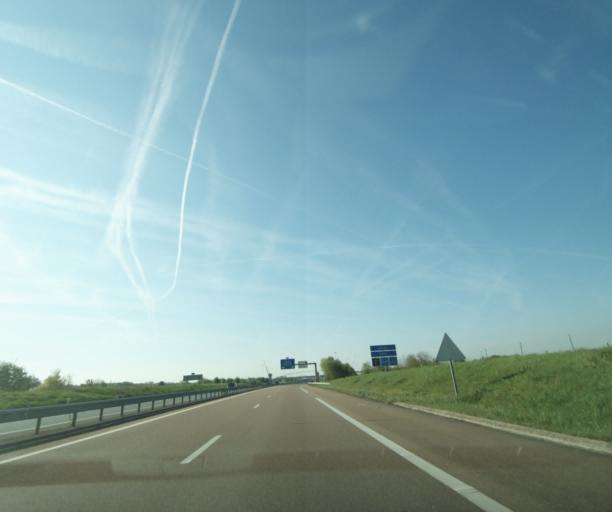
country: FR
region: Ile-de-France
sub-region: Departement de Seine-et-Marne
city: Souppes-sur-Loing
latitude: 48.1806
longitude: 2.7668
